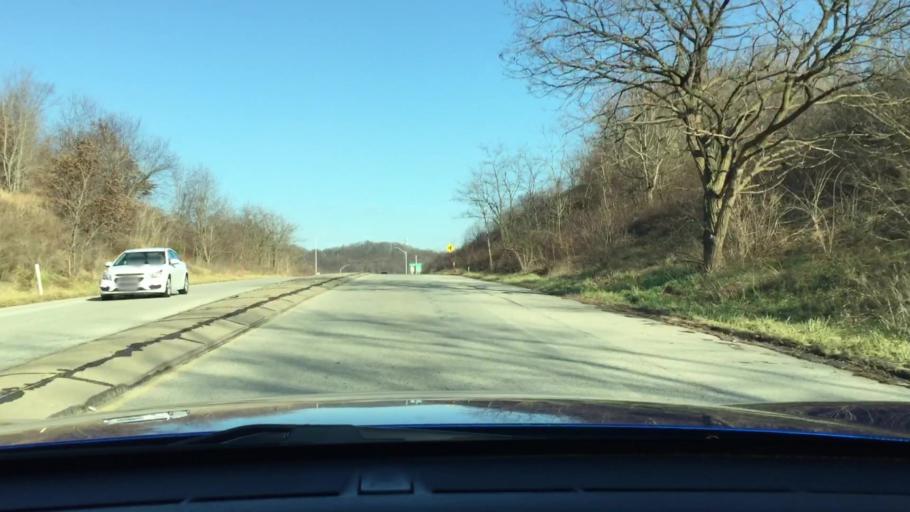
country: US
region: Pennsylvania
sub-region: Westmoreland County
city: New Stanton
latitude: 40.2306
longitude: -79.6064
